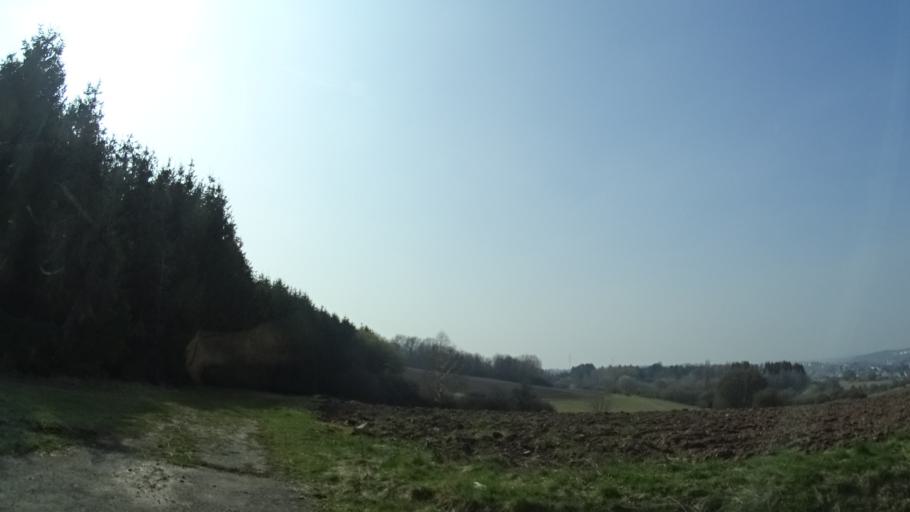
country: DE
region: Rheinland-Pfalz
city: Baumholder
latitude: 49.6029
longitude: 7.3496
